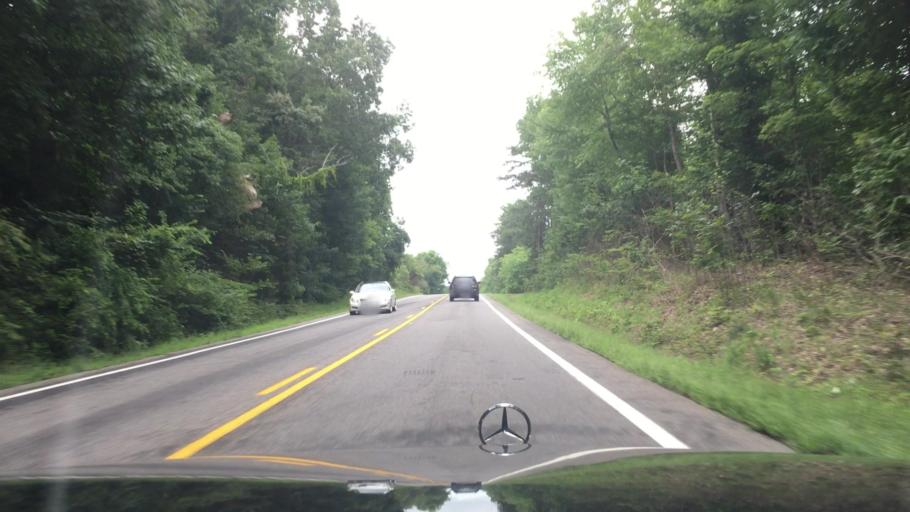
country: US
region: Virginia
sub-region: Prince Edward County
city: Farmville
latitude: 37.2738
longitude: -78.2615
